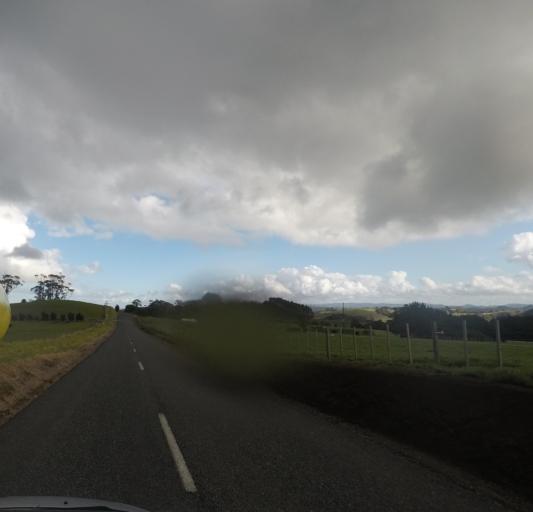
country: NZ
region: Auckland
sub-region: Auckland
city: Warkworth
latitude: -36.3693
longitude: 174.7658
